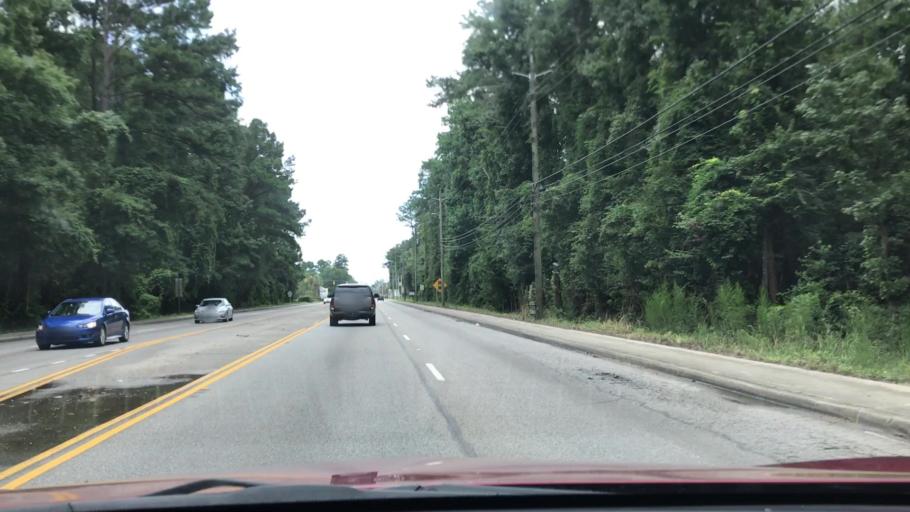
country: US
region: South Carolina
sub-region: Georgetown County
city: Georgetown
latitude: 33.3972
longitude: -79.2893
